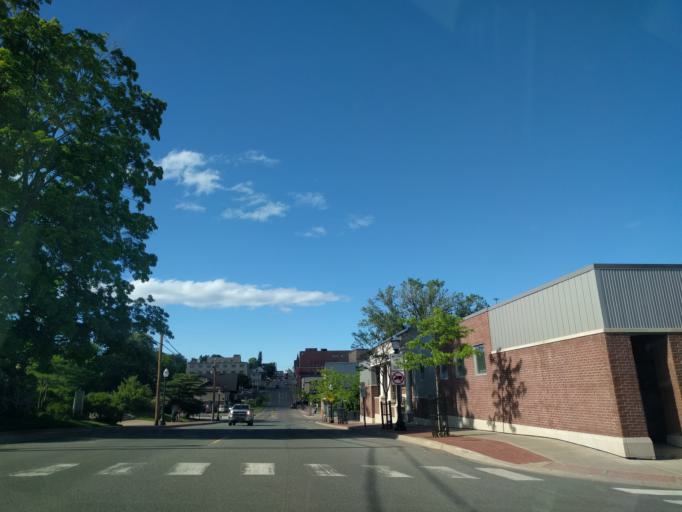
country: US
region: Michigan
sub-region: Marquette County
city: Marquette
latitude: 46.5411
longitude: -87.3961
